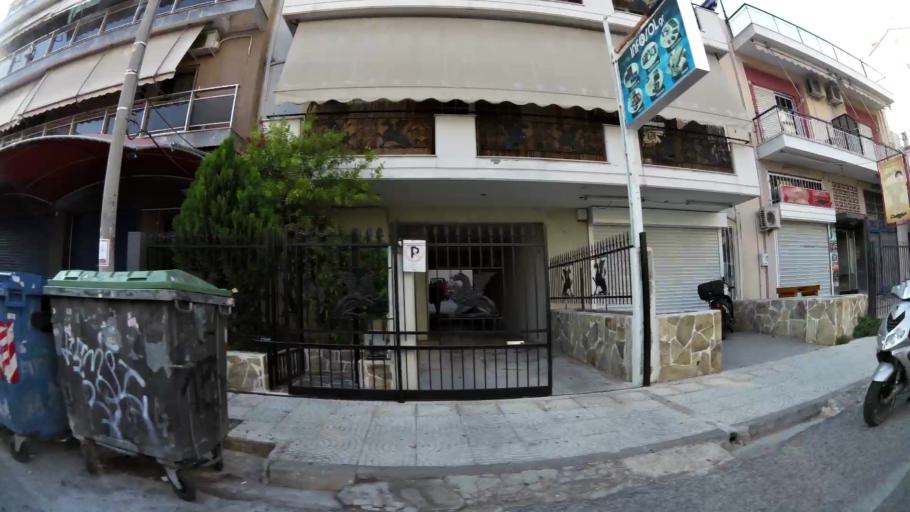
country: GR
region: Attica
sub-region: Nomarchia Athinas
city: Petroupolis
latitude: 38.0405
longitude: 23.6823
